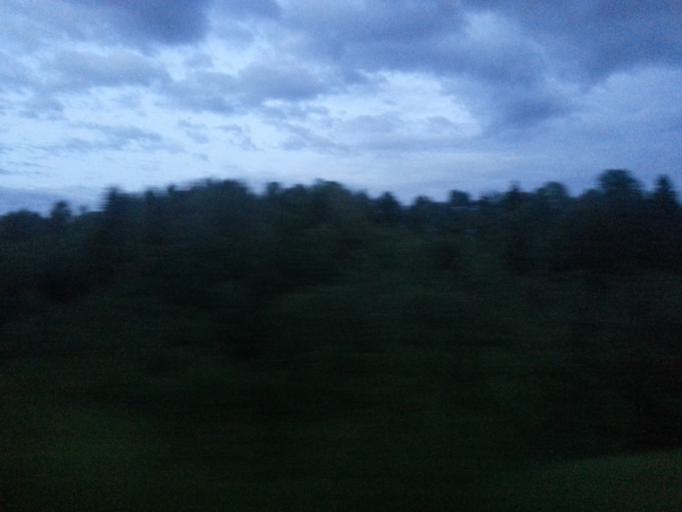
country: NO
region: Akershus
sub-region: Sorum
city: Frogner
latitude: 60.0197
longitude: 11.1183
